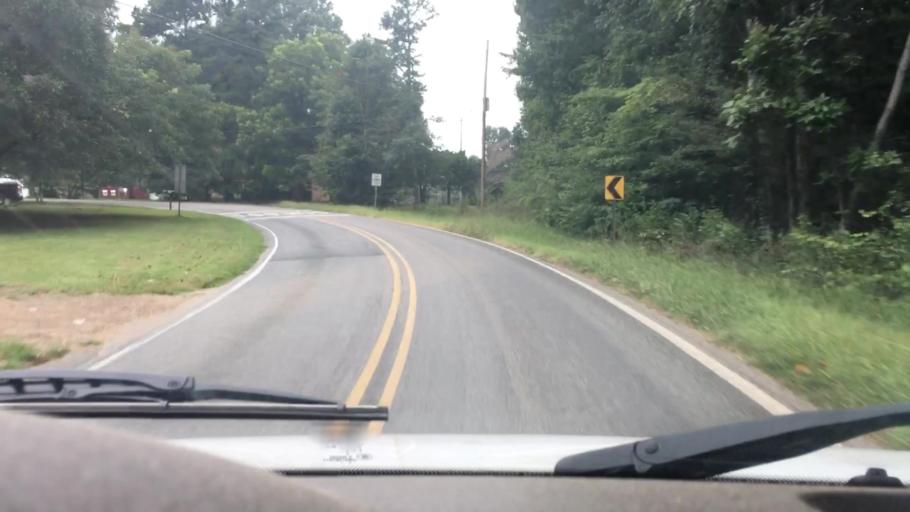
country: US
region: North Carolina
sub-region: Gaston County
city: Davidson
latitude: 35.5174
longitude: -80.8370
